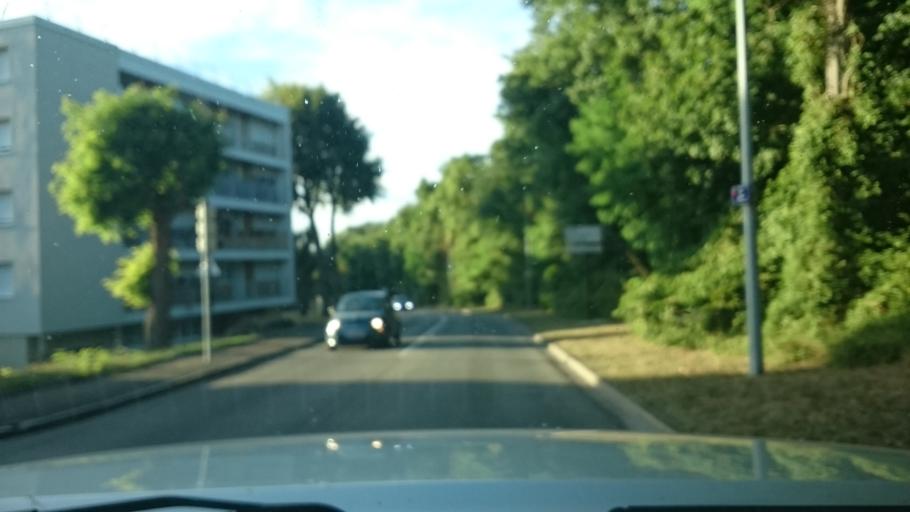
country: FR
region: Ile-de-France
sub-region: Departement de Seine-et-Marne
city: Samoreau
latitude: 48.4150
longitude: 2.7401
